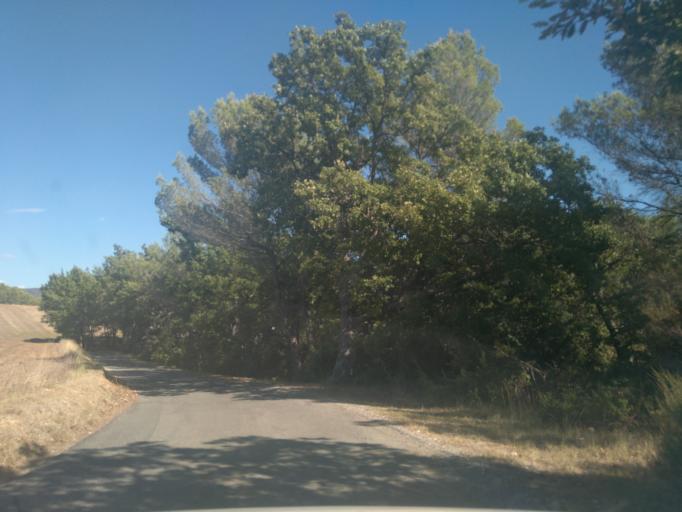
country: FR
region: Provence-Alpes-Cote d'Azur
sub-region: Departement du Var
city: Regusse
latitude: 43.6972
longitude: 6.1112
